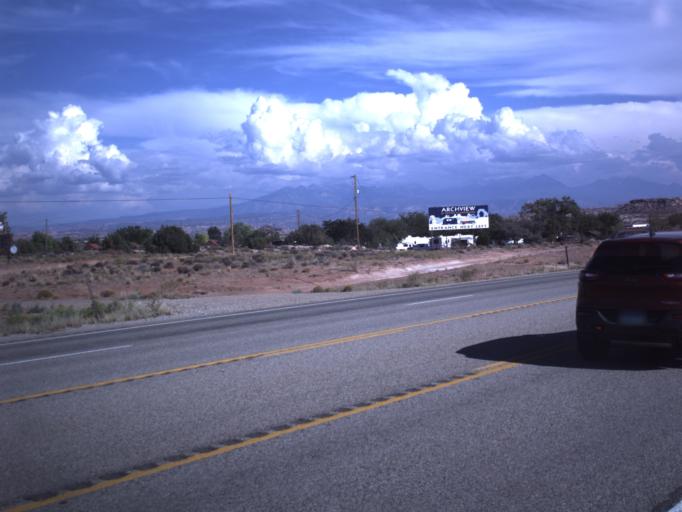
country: US
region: Utah
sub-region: Grand County
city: Moab
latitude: 38.6789
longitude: -109.6912
